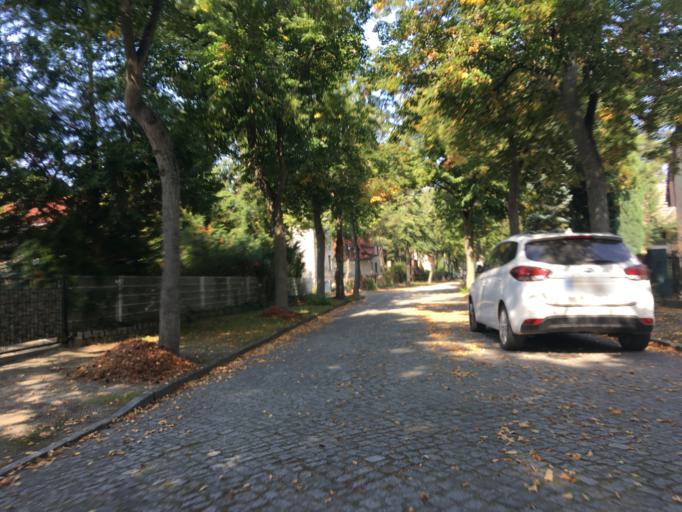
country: DE
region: Brandenburg
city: Zeuthen
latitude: 52.3673
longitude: 13.6330
